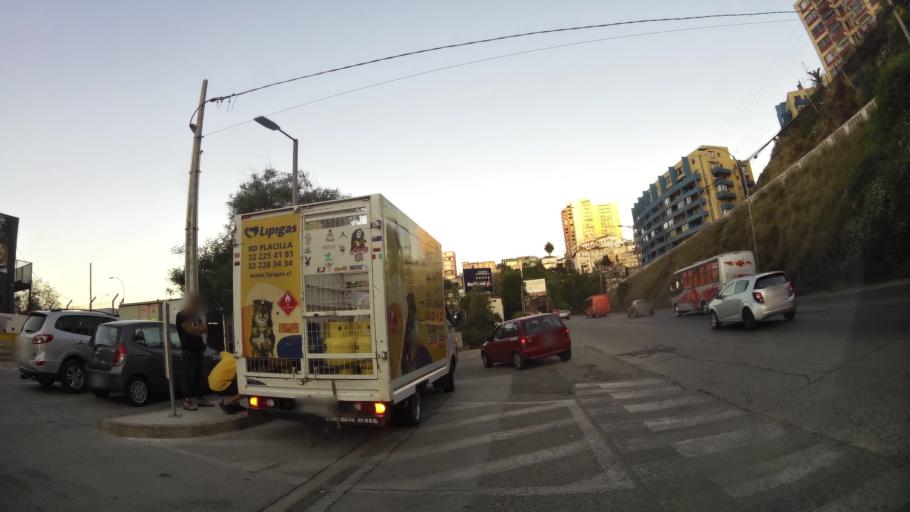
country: CL
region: Valparaiso
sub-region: Provincia de Valparaiso
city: Valparaiso
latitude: -33.0381
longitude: -71.6000
